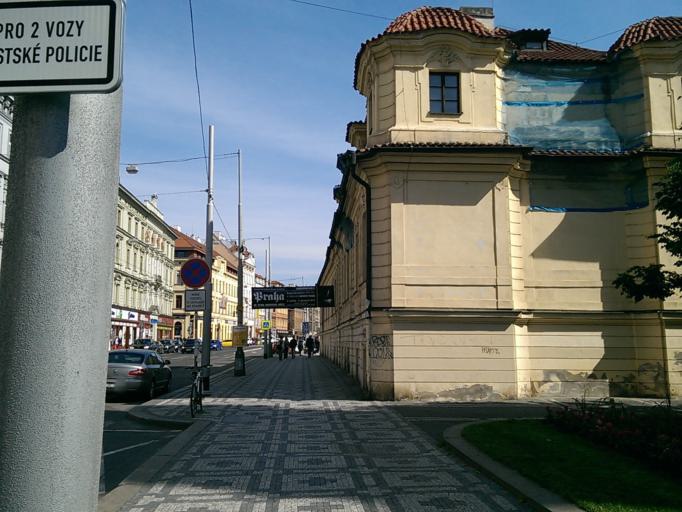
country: CZ
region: Praha
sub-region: Praha 1
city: Mala Strana
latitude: 50.0733
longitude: 14.4039
